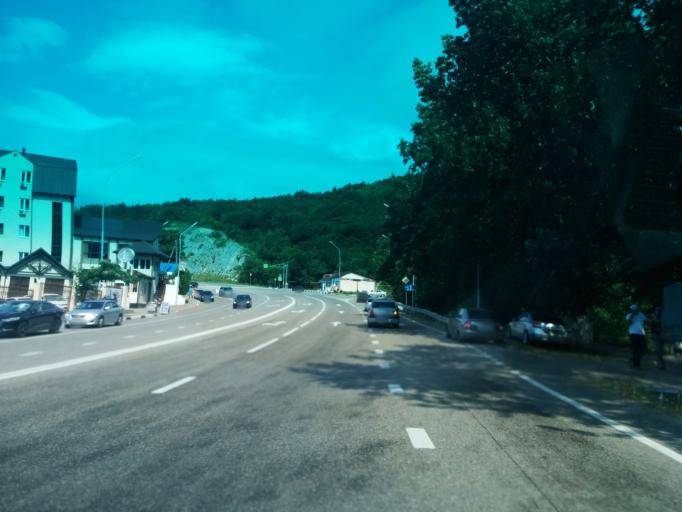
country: RU
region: Krasnodarskiy
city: Nebug
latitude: 44.1657
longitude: 38.9996
